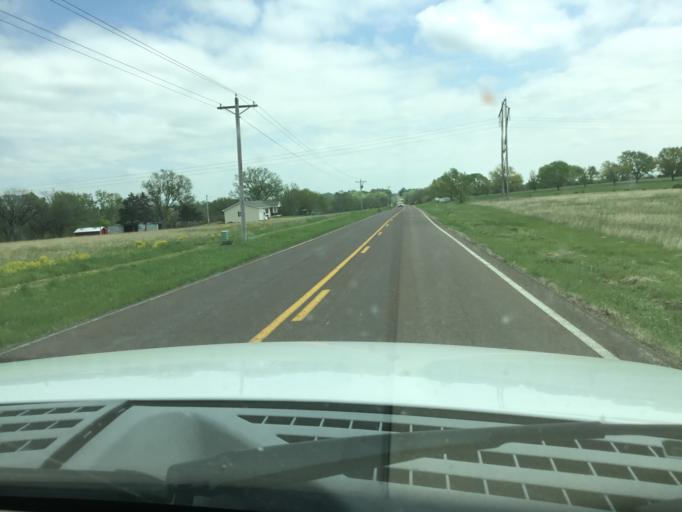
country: US
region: Kansas
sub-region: Shawnee County
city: Auburn
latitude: 38.9562
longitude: -95.8048
